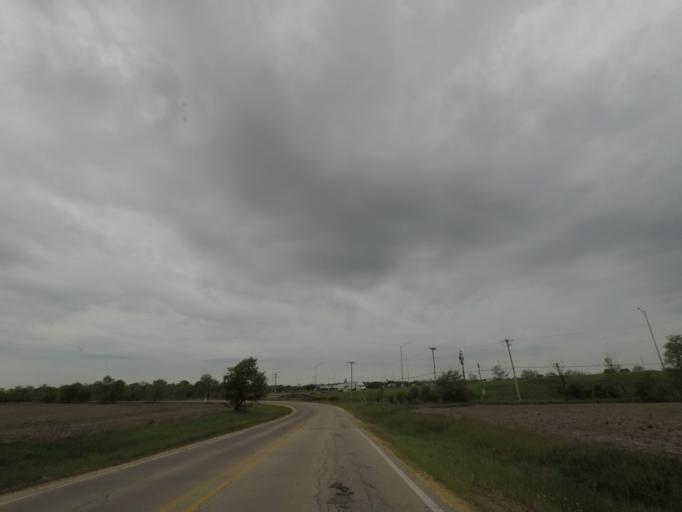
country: US
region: Illinois
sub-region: Winnebago County
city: Roscoe
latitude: 42.4558
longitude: -88.9922
